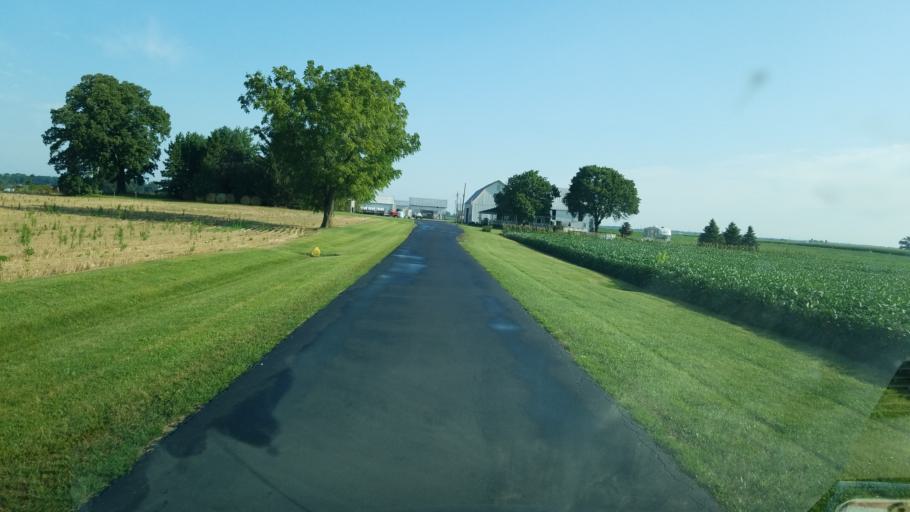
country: US
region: Ohio
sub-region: Crawford County
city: Bucyrus
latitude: 40.7767
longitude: -82.9178
